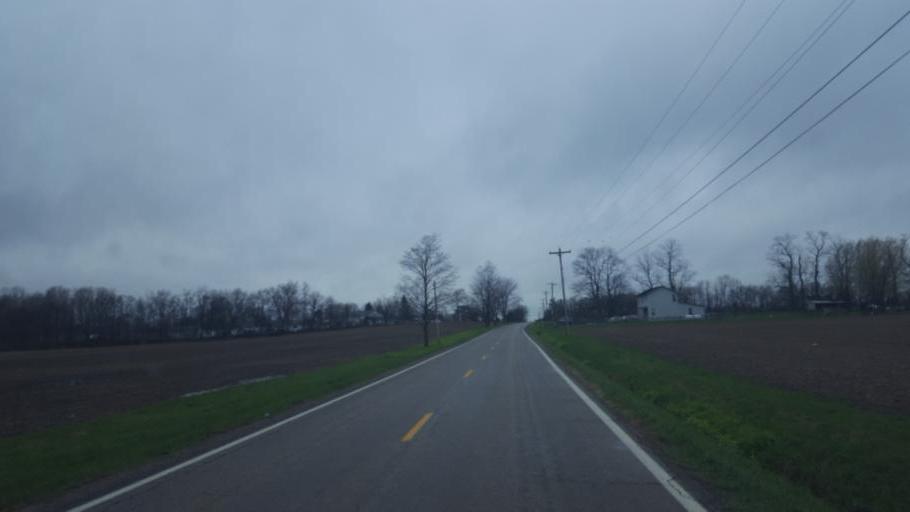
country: US
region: Ohio
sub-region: Morrow County
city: Mount Gilead
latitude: 40.4817
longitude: -82.8273
